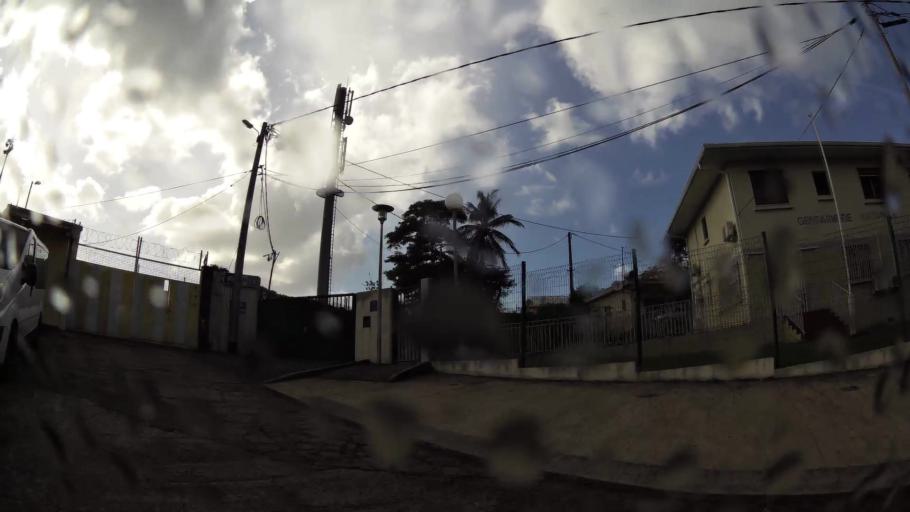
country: MQ
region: Martinique
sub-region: Martinique
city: Les Trois-Ilets
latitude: 14.5377
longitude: -61.0363
